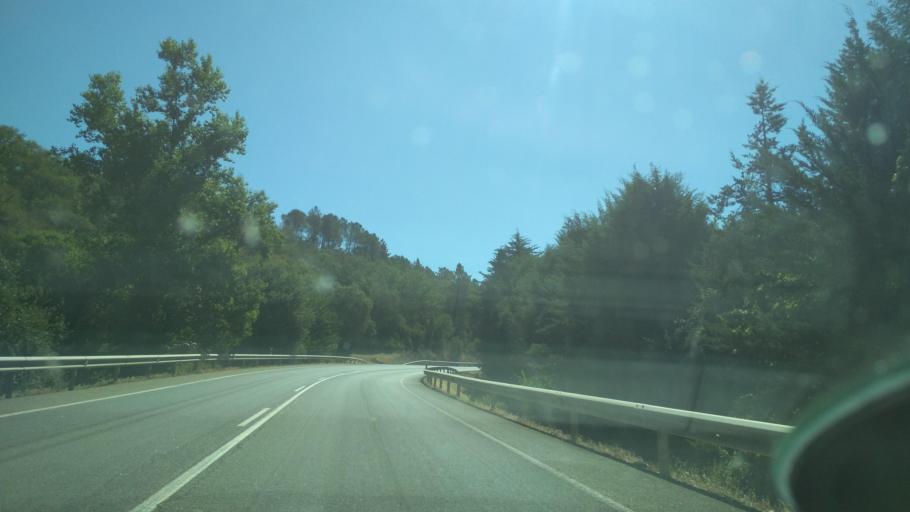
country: ES
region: Andalusia
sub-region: Provincia de Huelva
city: Fuenteheridos
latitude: 37.9170
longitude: -6.6728
